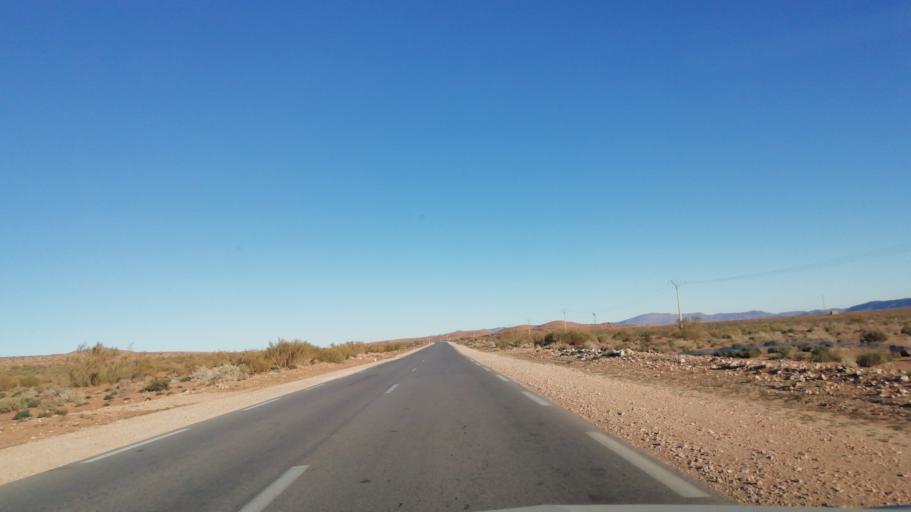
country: DZ
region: El Bayadh
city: El Abiodh Sidi Cheikh
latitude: 33.1610
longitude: 0.3941
